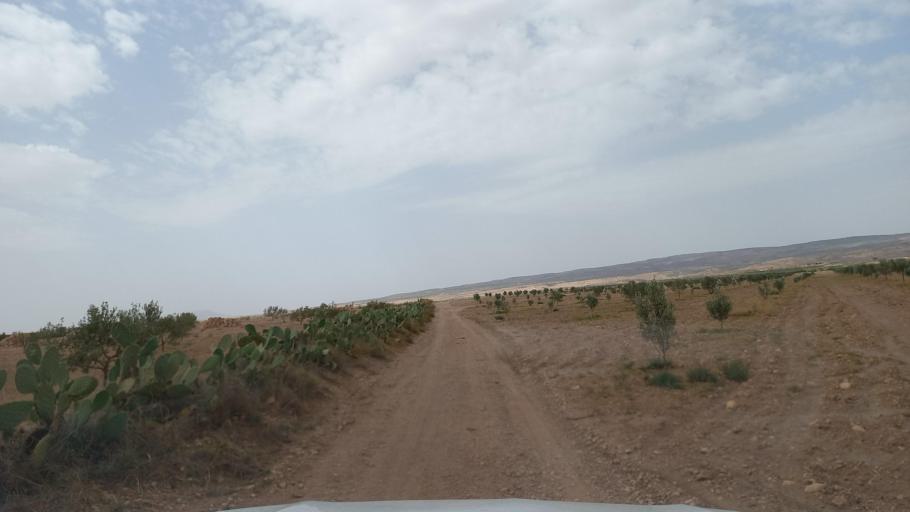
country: TN
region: Al Qasrayn
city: Kasserine
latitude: 35.2919
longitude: 9.0032
